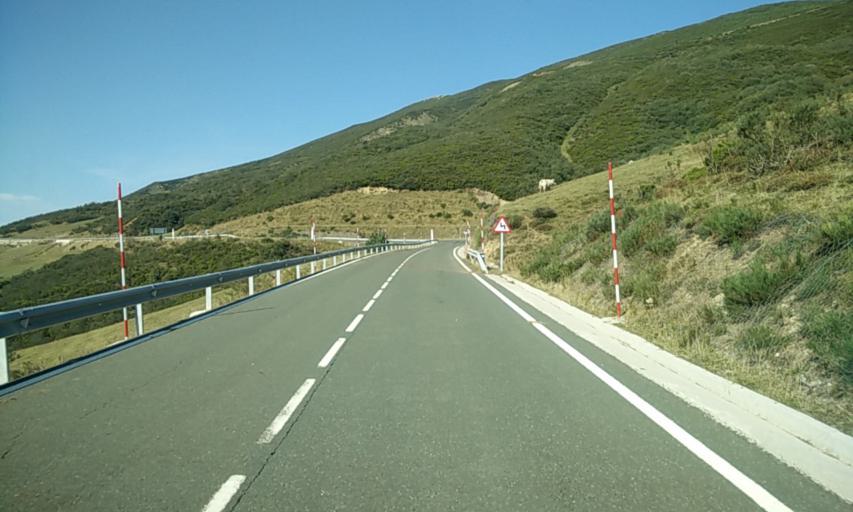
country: ES
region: Cantabria
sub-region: Provincia de Cantabria
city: Camaleno
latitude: 43.0718
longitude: -4.7471
